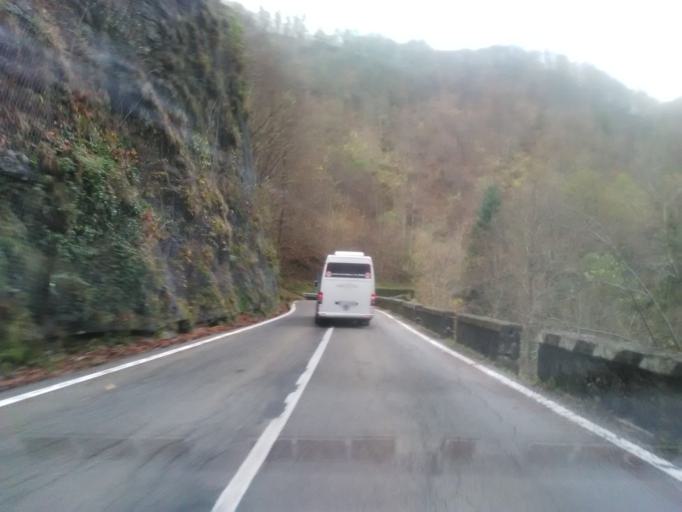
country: IT
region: Piedmont
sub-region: Provincia di Vercelli
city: Sabbia
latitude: 45.8433
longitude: 8.2494
